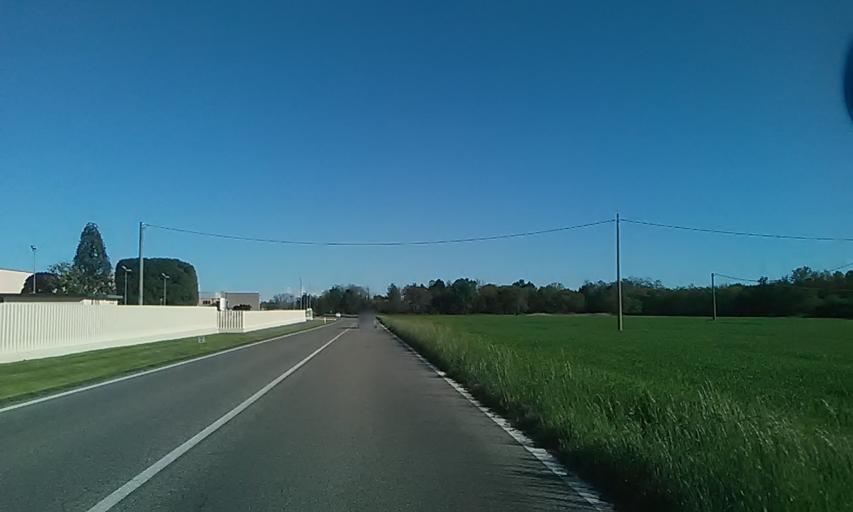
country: IT
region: Piedmont
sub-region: Provincia di Novara
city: Cavaglietto
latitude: 45.6073
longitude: 8.5241
